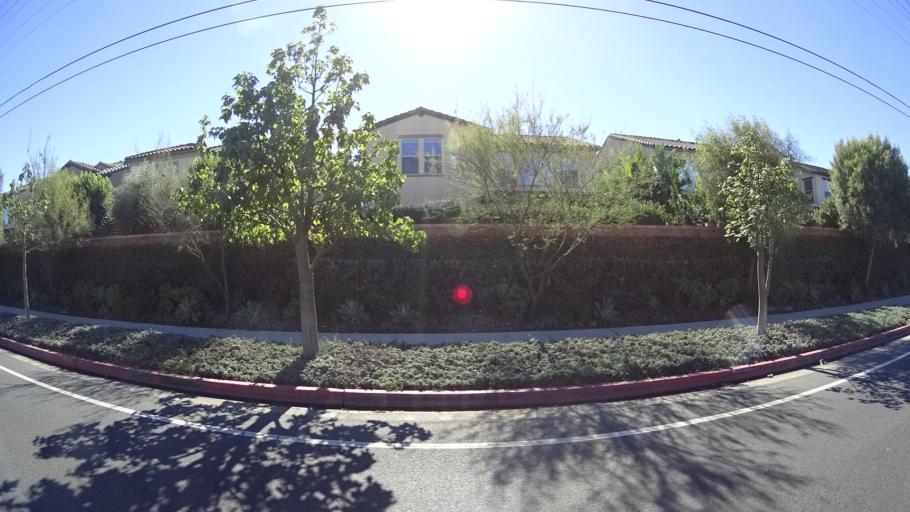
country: US
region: California
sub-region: Orange County
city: Cypress
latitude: 33.8171
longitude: -118.0236
